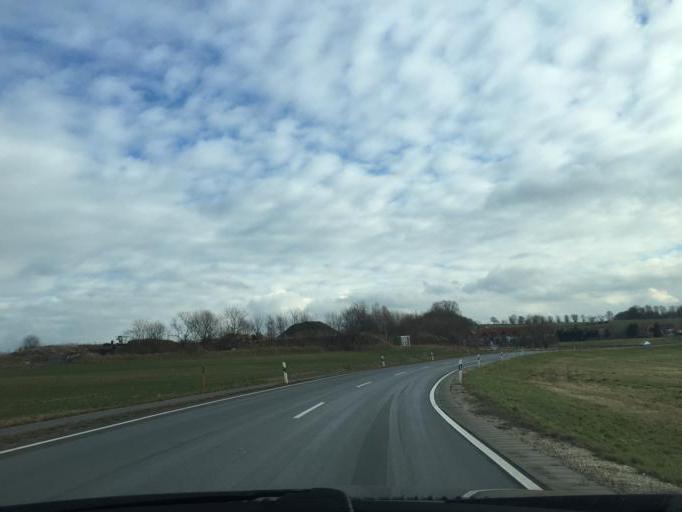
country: DE
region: Saxony
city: Wachau
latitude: 51.1655
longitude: 13.8710
